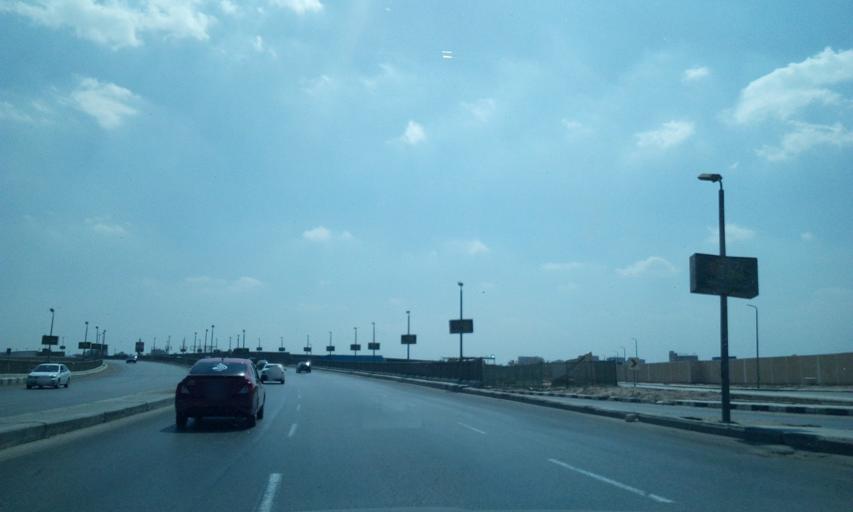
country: EG
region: Muhafazat al Qahirah
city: Cairo
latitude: 30.0825
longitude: 31.3628
